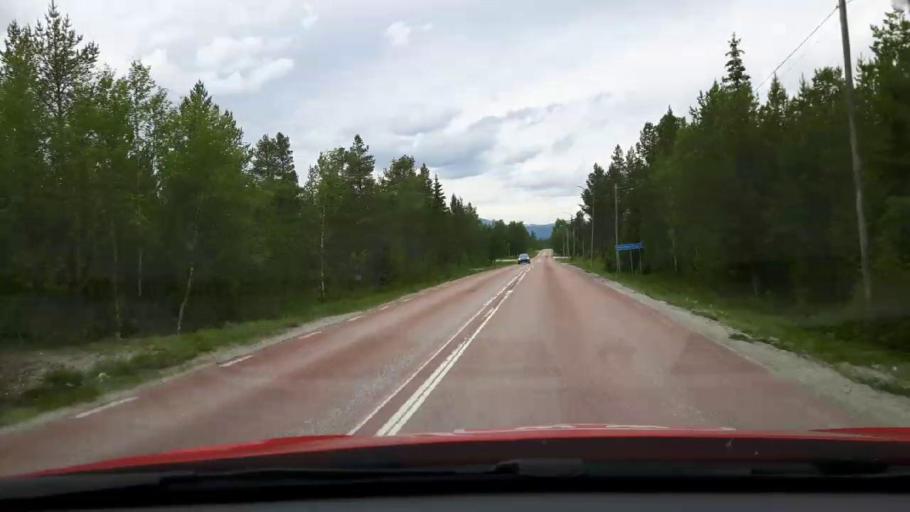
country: NO
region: Hedmark
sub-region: Engerdal
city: Engerdal
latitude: 62.5037
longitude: 12.6217
